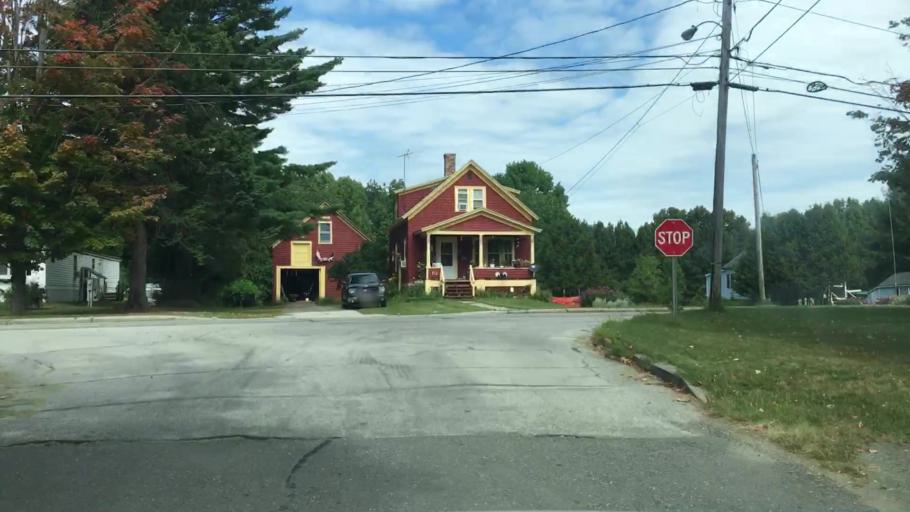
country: US
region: Maine
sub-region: Piscataquis County
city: Dover-Foxcroft
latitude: 45.1908
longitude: -69.2232
